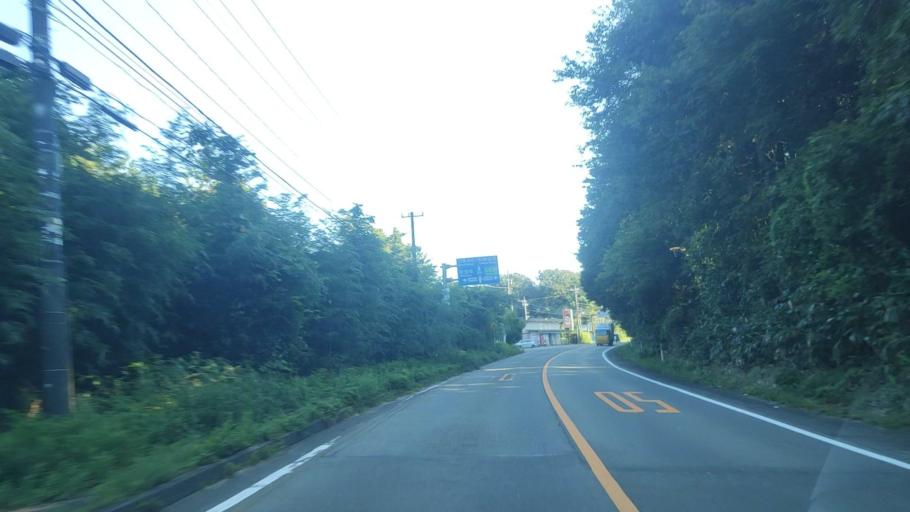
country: JP
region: Ishikawa
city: Nanao
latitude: 37.1326
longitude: 136.8636
